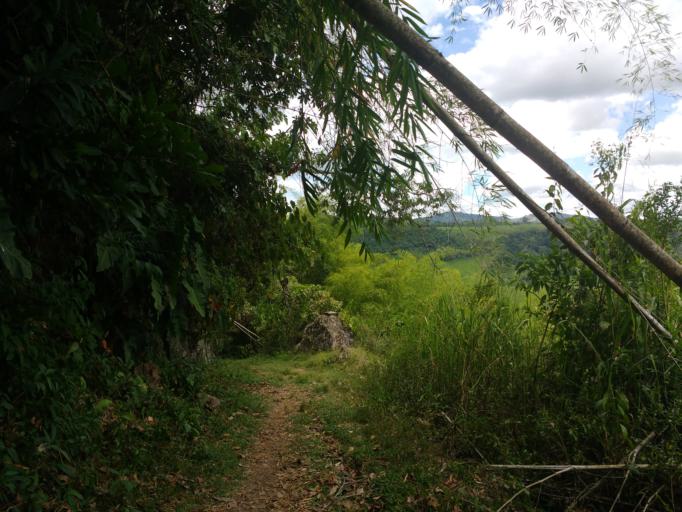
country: CO
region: Valle del Cauca
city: Alcala
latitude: 4.6725
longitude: -75.8172
